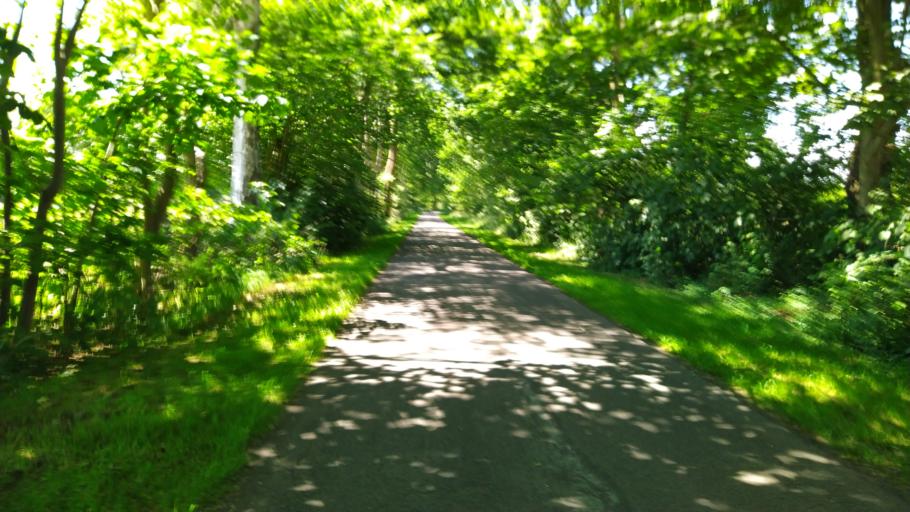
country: DE
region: Lower Saxony
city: Estorf
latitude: 53.5626
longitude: 9.2136
